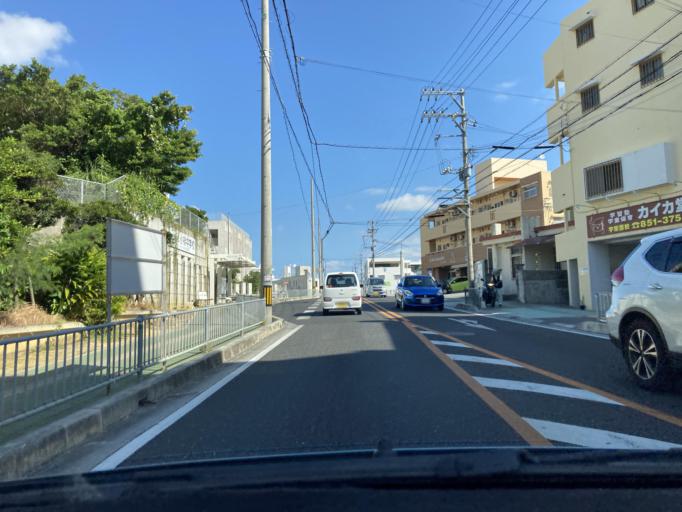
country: JP
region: Okinawa
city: Tomigusuku
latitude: 26.1885
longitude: 127.6680
